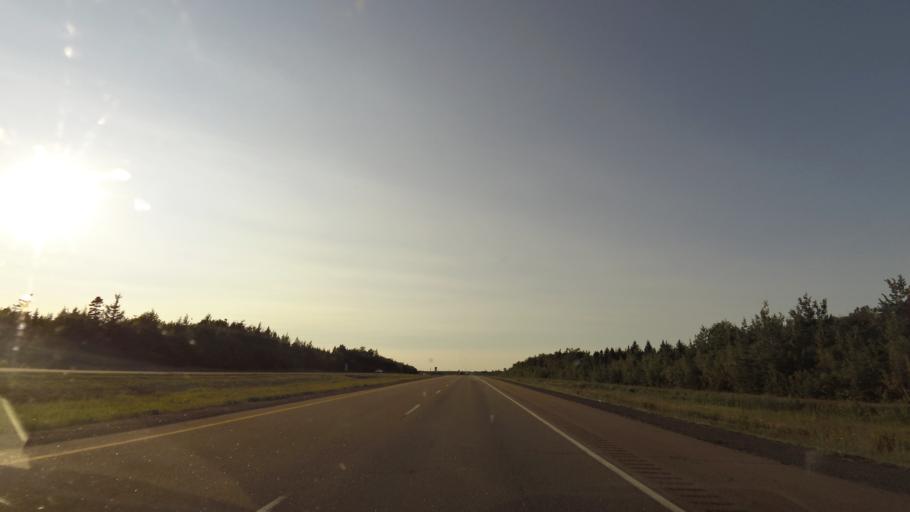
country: CA
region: New Brunswick
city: Dieppe
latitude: 46.1201
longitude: -64.6289
